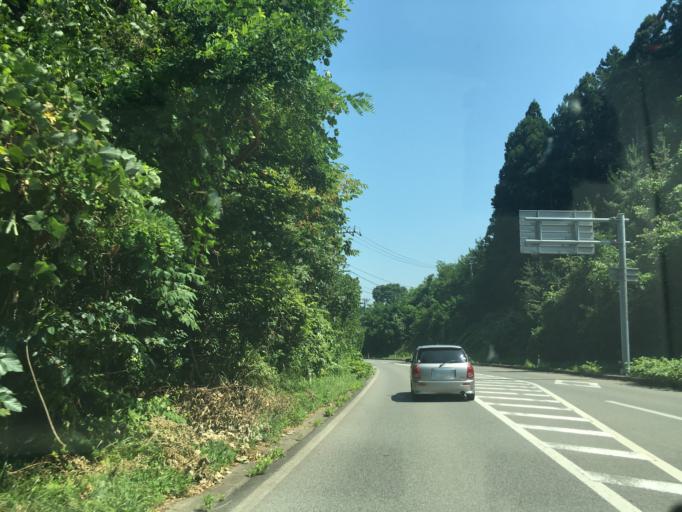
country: JP
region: Akita
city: Tenno
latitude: 39.9722
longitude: 139.7392
